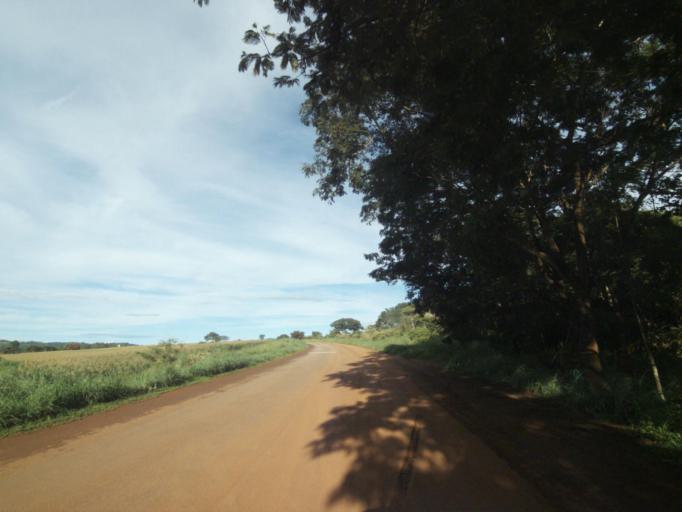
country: BR
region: Goias
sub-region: Jaragua
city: Jaragua
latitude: -15.9087
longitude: -49.5584
